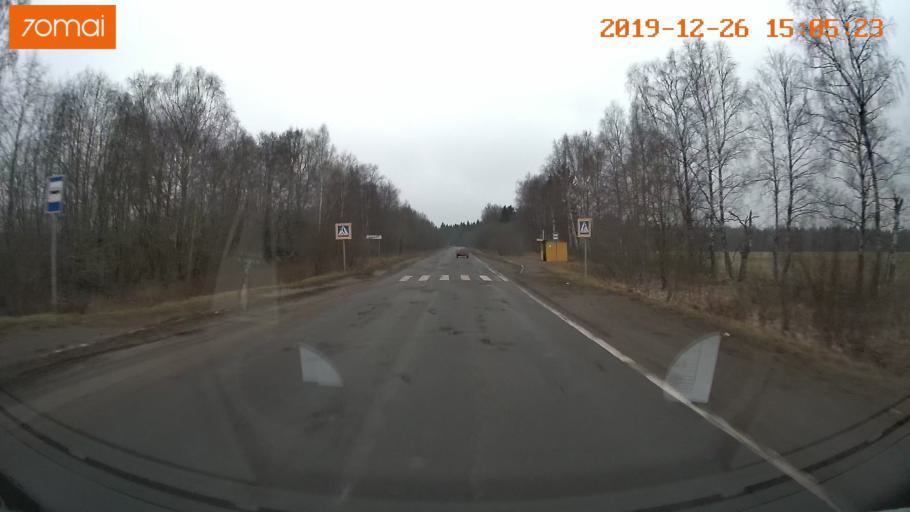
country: RU
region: Jaroslavl
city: Rybinsk
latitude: 58.1896
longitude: 38.8522
